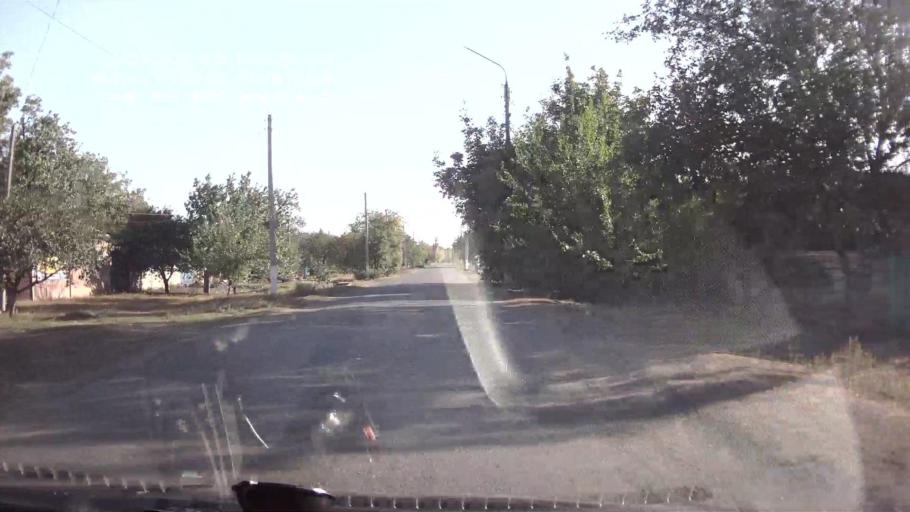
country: RU
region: Rostov
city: Gigant
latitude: 46.5212
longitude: 41.1911
